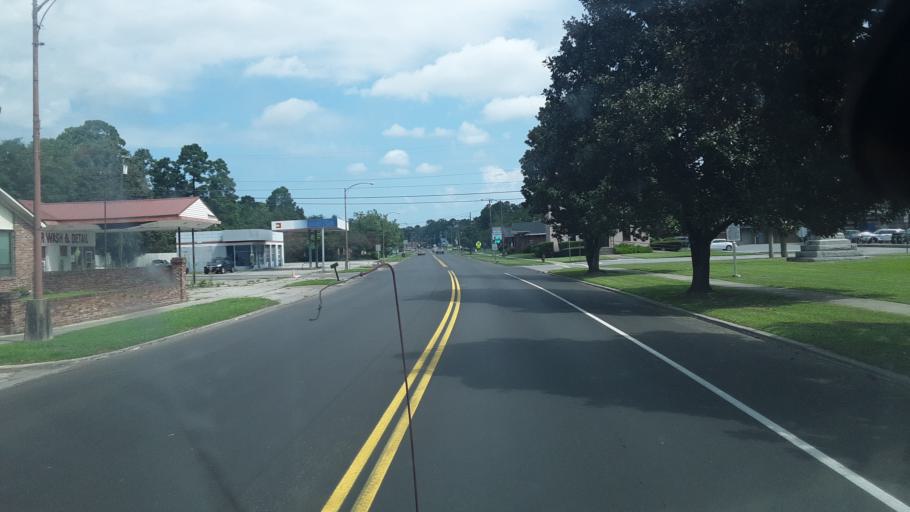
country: US
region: South Carolina
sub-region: Bamberg County
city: Bamberg
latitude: 33.2979
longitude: -81.0346
